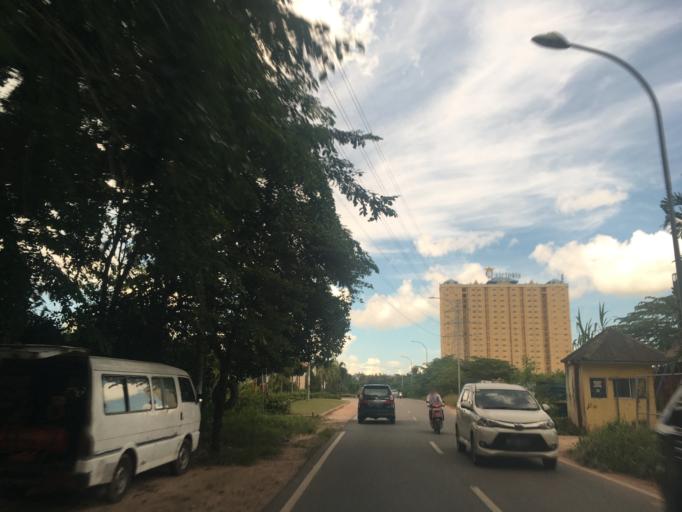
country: SG
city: Singapore
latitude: 1.1207
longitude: 104.0263
